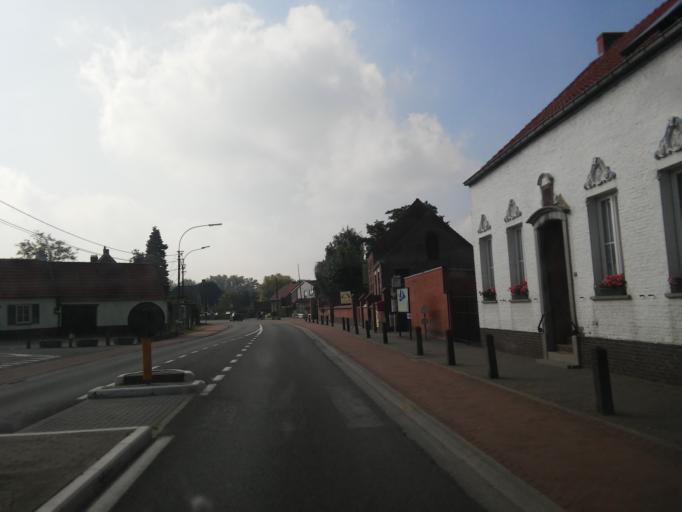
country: BE
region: Flanders
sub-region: Provincie Oost-Vlaanderen
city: Berlare
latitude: 51.0416
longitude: 3.9834
